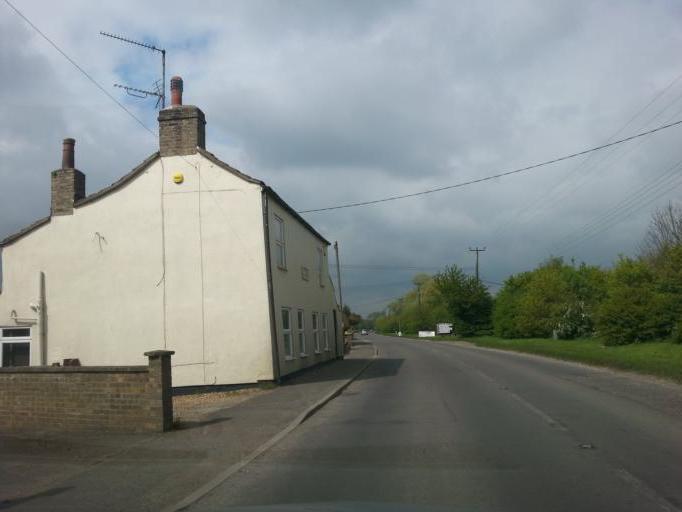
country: GB
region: England
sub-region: Norfolk
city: Outwell
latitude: 52.6118
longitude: 0.2330
